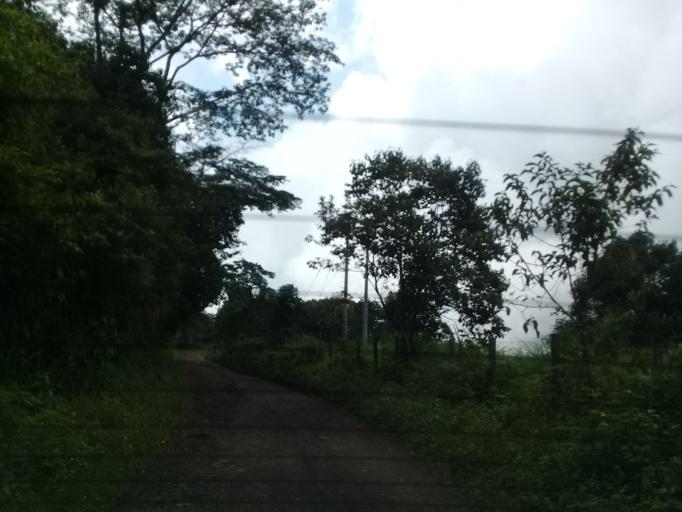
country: CO
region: Cundinamarca
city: Quipile
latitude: 4.7199
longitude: -74.5517
